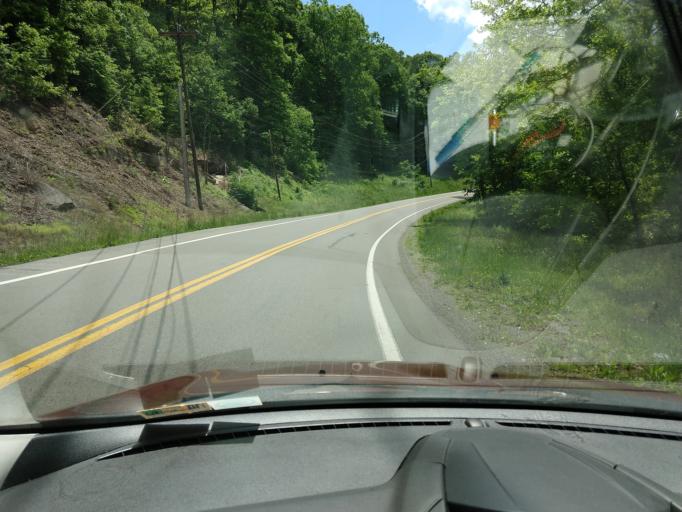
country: US
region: West Virginia
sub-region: Gilmer County
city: Glenville
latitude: 38.8884
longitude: -80.7198
